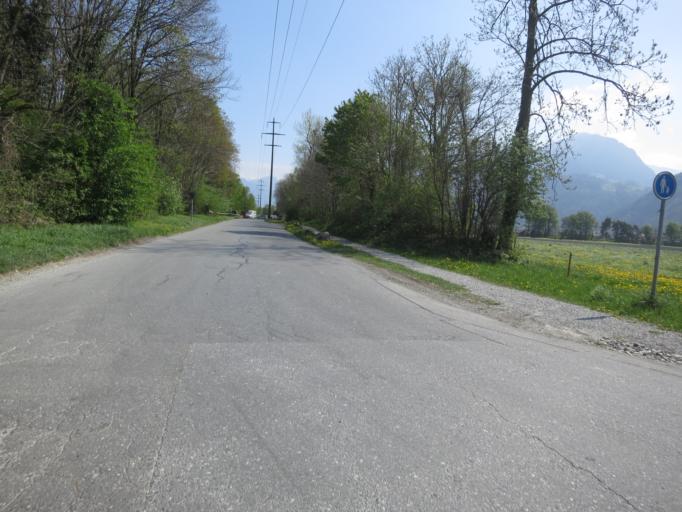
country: CH
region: Saint Gallen
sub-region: Wahlkreis Sarganserland
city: Bad Ragaz
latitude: 47.0212
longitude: 9.4982
